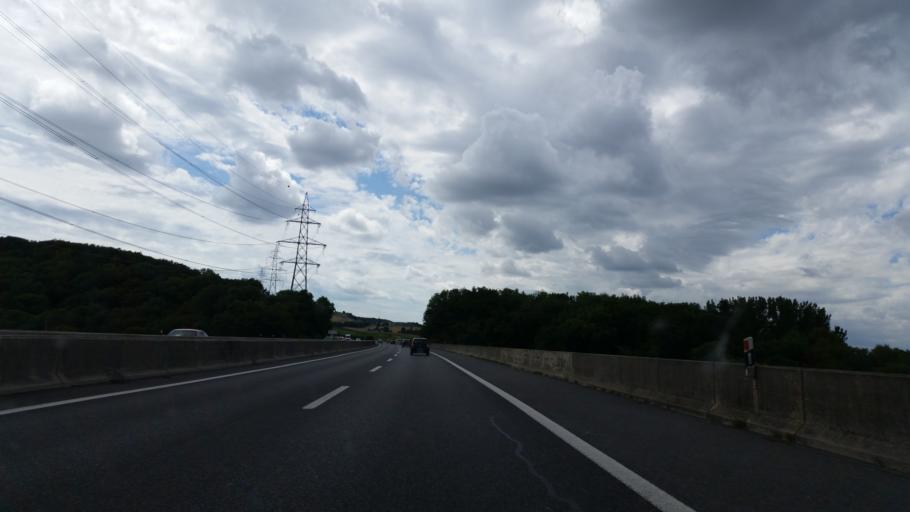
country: CH
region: Vaud
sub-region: Jura-Nord vaudois District
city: Chavornay
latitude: 46.6967
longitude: 6.5744
